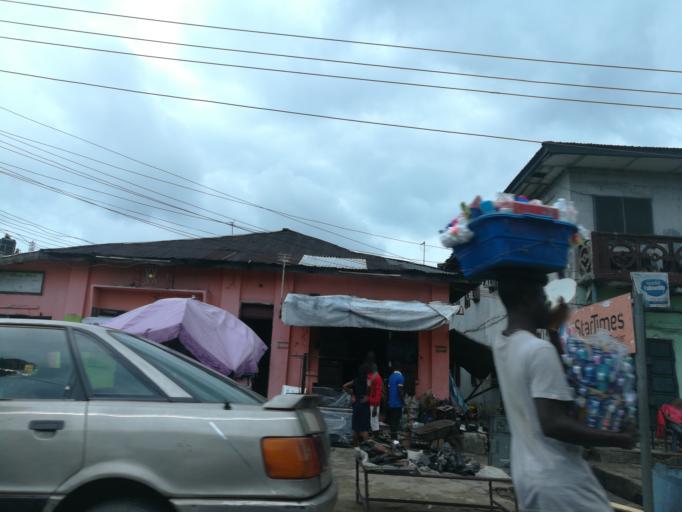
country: NG
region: Rivers
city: Port Harcourt
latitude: 4.7557
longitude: 7.0377
